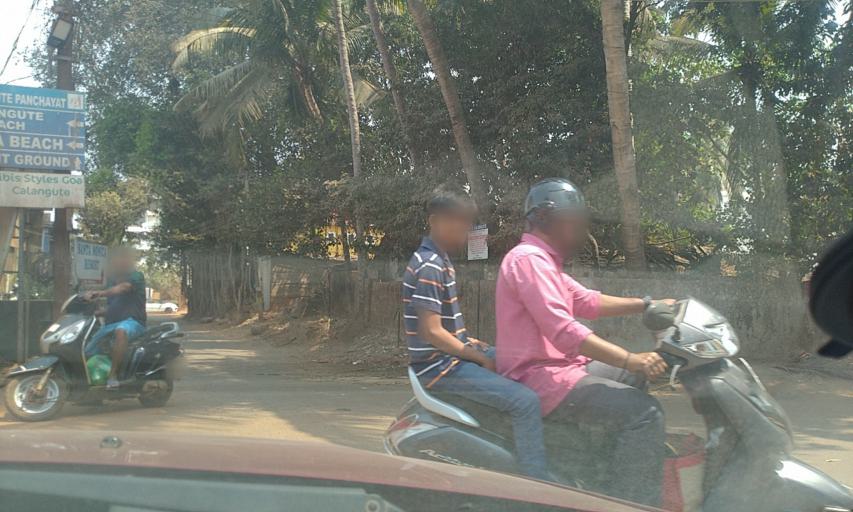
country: IN
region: Goa
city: Calangute
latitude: 15.5390
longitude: 73.7631
